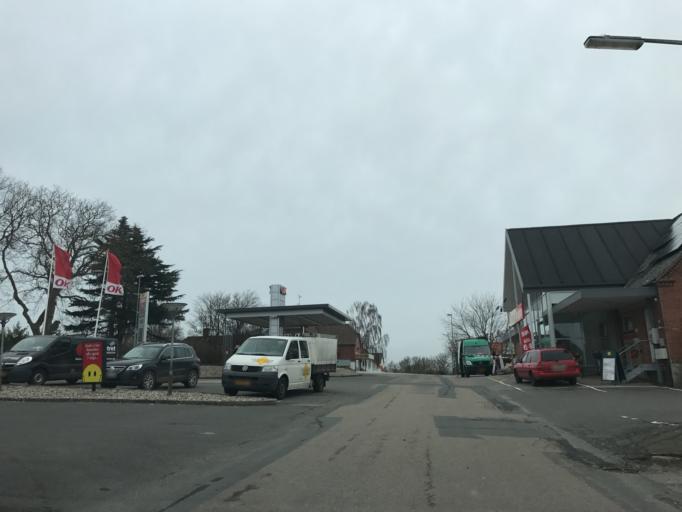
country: DK
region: South Denmark
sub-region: Langeland Kommune
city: Rudkobing
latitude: 54.9579
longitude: 10.8011
